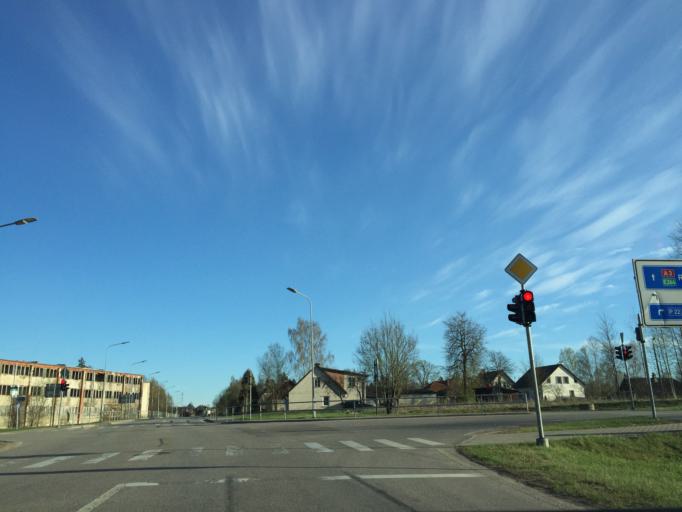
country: LV
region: Valkas Rajons
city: Valka
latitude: 57.7805
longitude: 25.9915
